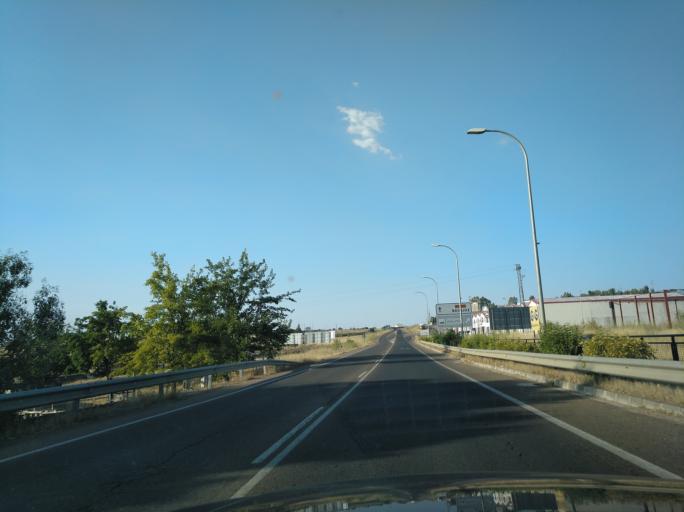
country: ES
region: Extremadura
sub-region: Provincia de Badajoz
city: Olivenza
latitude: 38.6937
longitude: -7.0914
